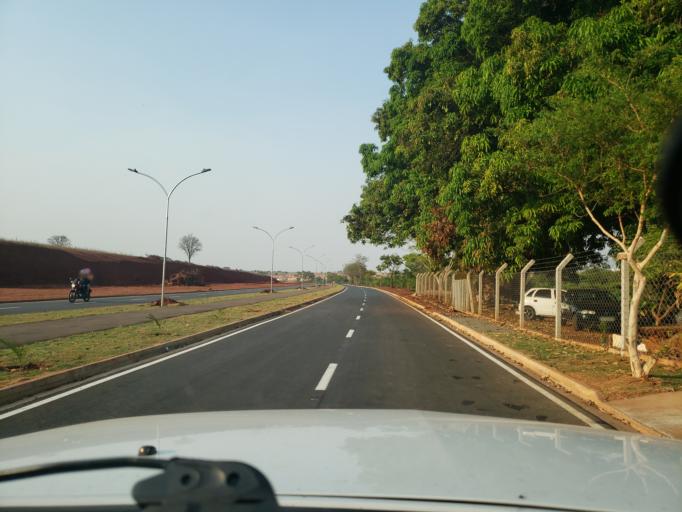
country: BR
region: Sao Paulo
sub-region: Moji-Guacu
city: Mogi-Gaucu
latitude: -22.3230
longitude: -46.9482
